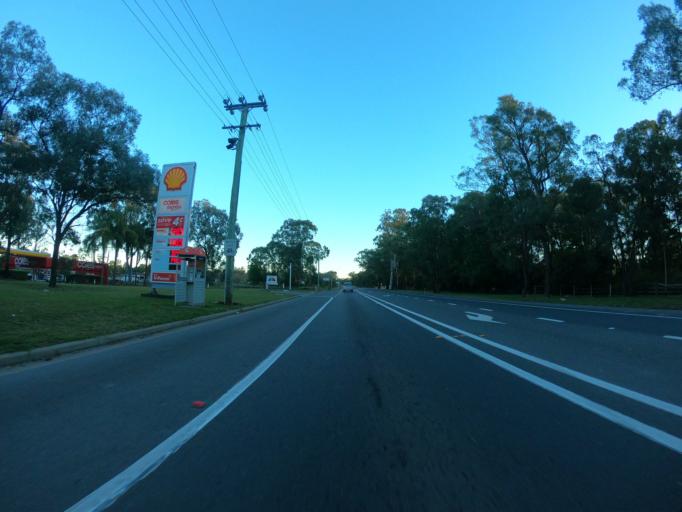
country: AU
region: New South Wales
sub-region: Hawkesbury
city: South Windsor
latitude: -33.6645
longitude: 150.8001
